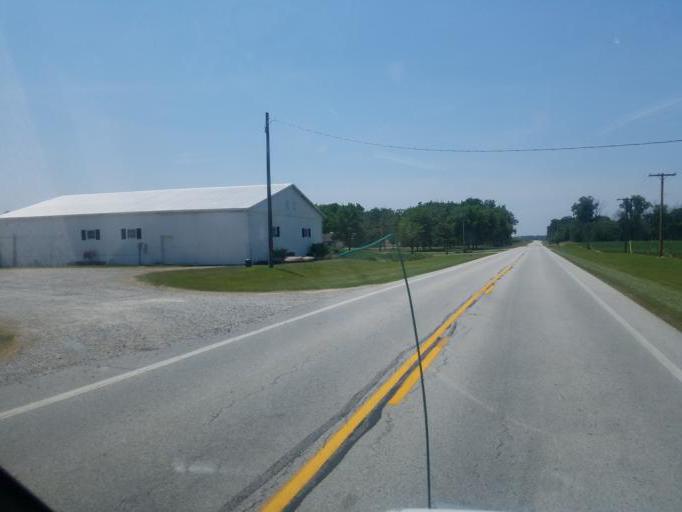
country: US
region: Ohio
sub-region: Shelby County
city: Fort Loramie
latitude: 40.3490
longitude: -84.3821
